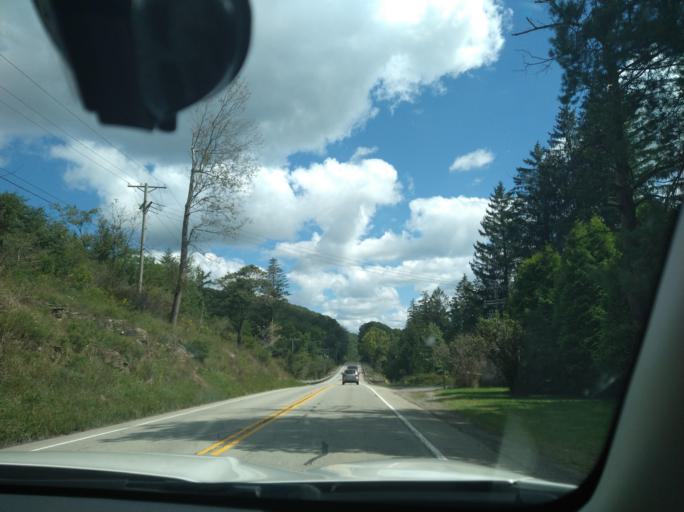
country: US
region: Pennsylvania
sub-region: Somerset County
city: Somerset
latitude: 40.0660
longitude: -79.2441
